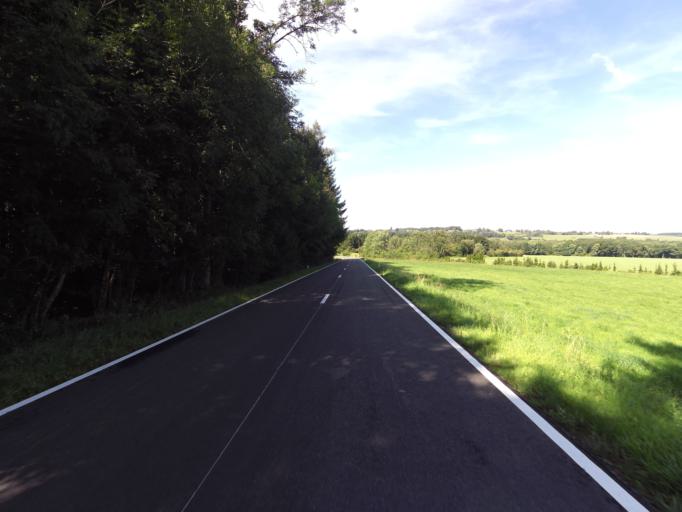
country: BE
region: Wallonia
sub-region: Province du Luxembourg
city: Nassogne
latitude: 50.1277
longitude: 5.3690
